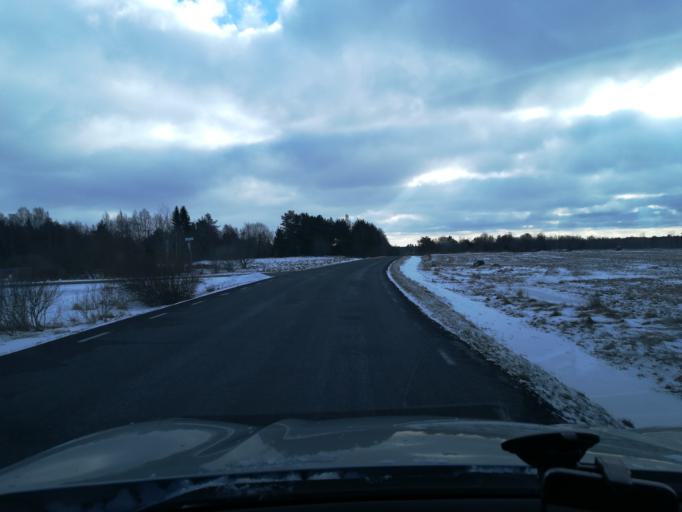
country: EE
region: Harju
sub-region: Harku vald
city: Tabasalu
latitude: 59.4217
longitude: 24.4210
